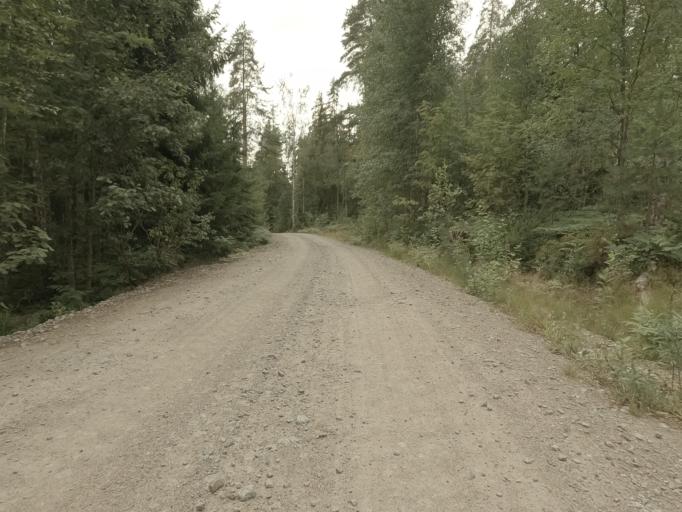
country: RU
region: Leningrad
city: Kamennogorsk
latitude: 60.9876
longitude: 29.1842
